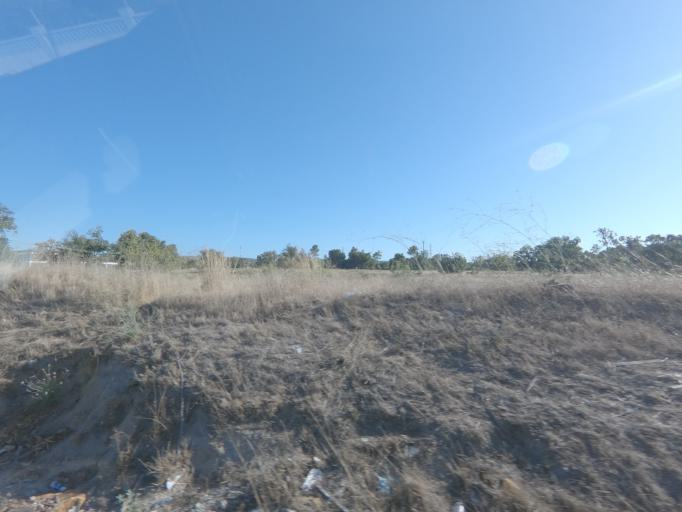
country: PT
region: Setubal
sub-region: Palmela
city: Quinta do Anjo
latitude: 38.5931
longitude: -8.9240
